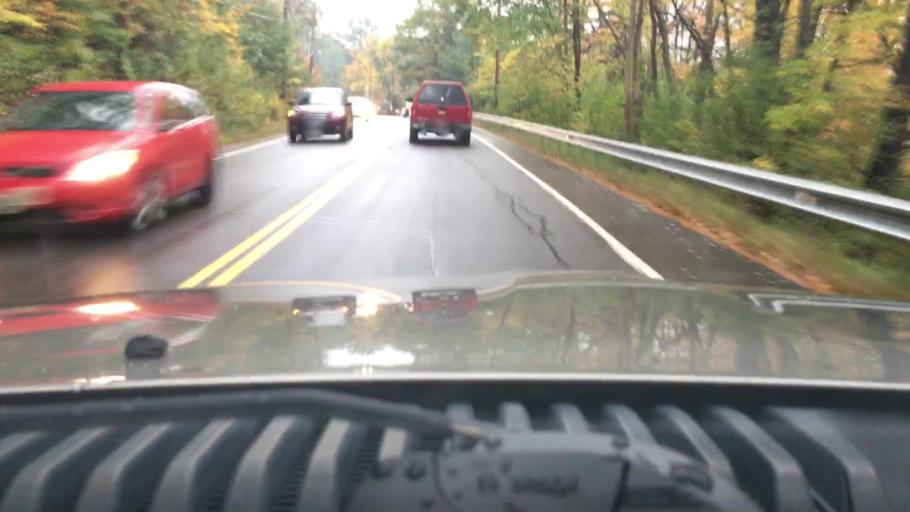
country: US
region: New Hampshire
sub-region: Hillsborough County
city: Pinardville
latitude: 43.0266
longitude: -71.4833
